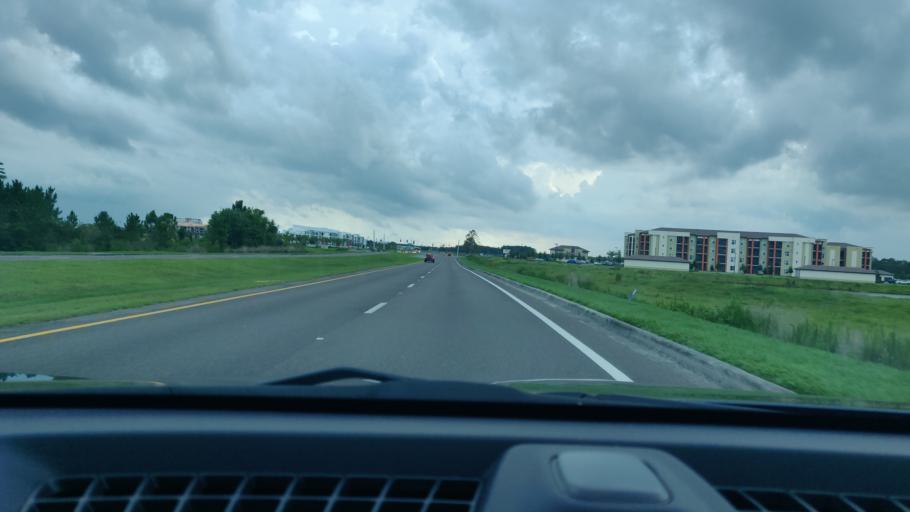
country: US
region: Florida
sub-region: Orange County
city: Hunters Creek
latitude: 28.3455
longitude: -81.4667
